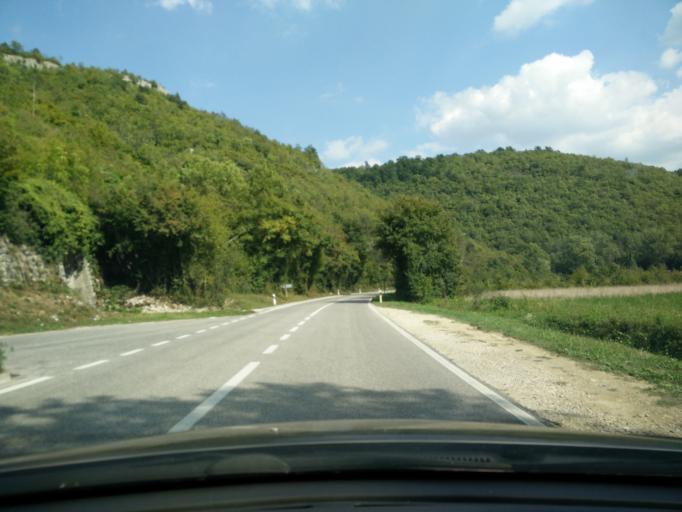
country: HR
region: Istarska
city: Buzet
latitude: 45.3935
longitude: 13.9092
